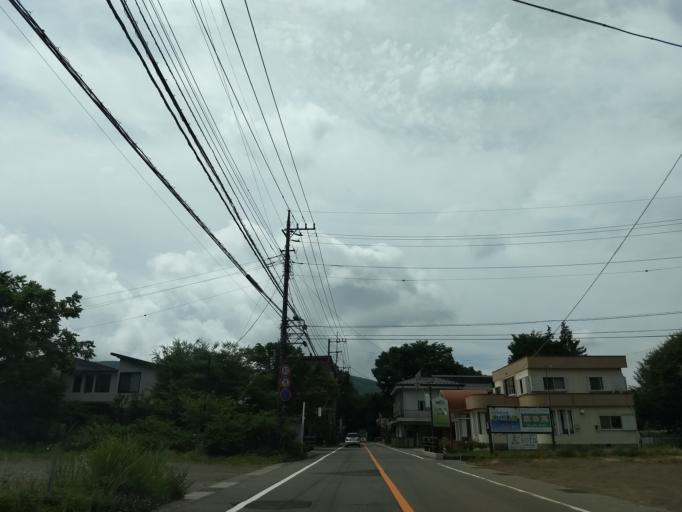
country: JP
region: Shizuoka
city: Gotemba
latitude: 35.4247
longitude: 138.9044
